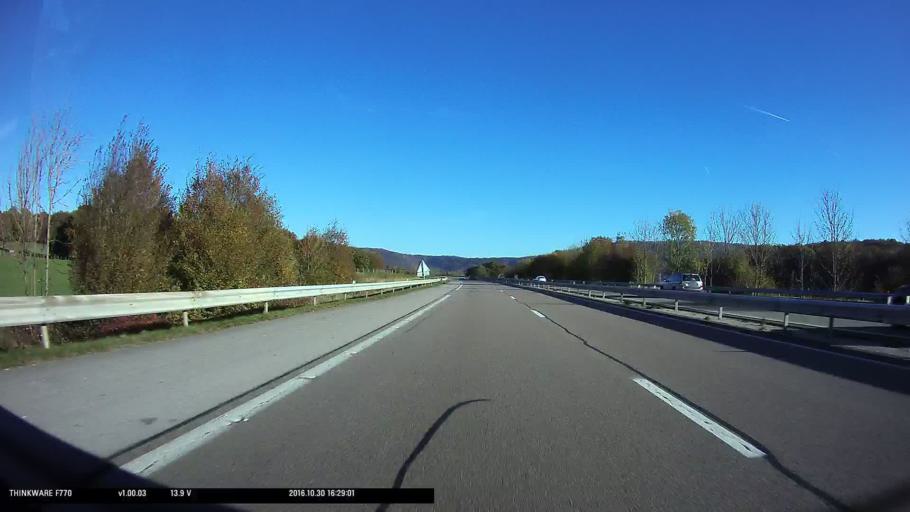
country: FR
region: Franche-Comte
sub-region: Departement du Doubs
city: Roulans
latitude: 47.3413
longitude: 6.2758
